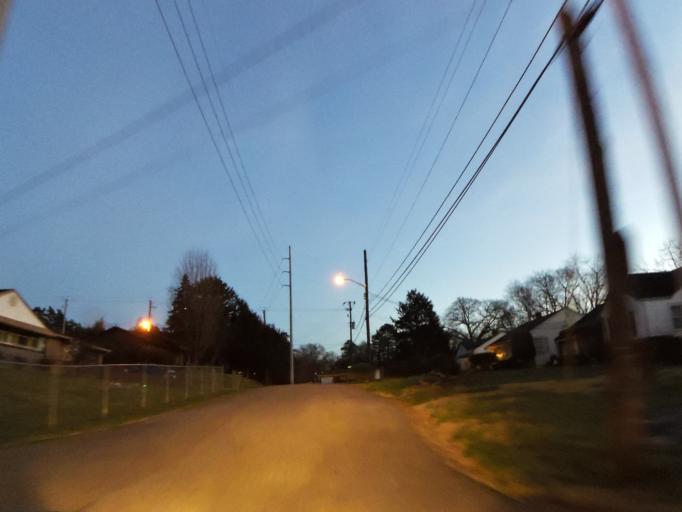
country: US
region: Tennessee
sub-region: Knox County
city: Knoxville
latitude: 35.9921
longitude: -83.8828
